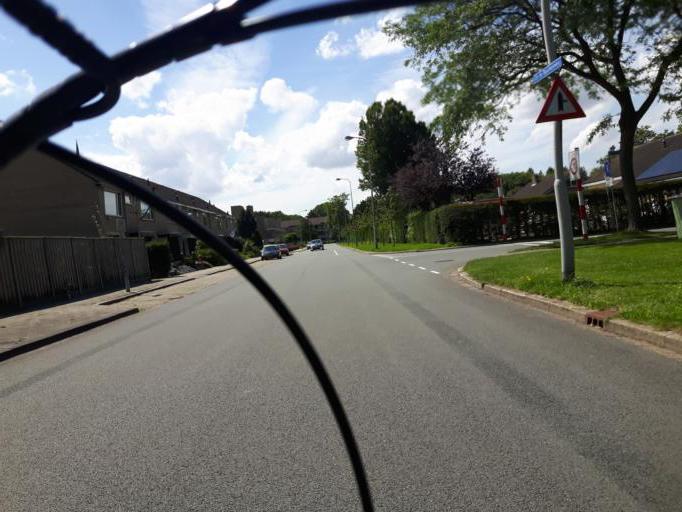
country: NL
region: Zeeland
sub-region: Gemeente Goes
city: Goes
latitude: 51.5087
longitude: 3.9055
